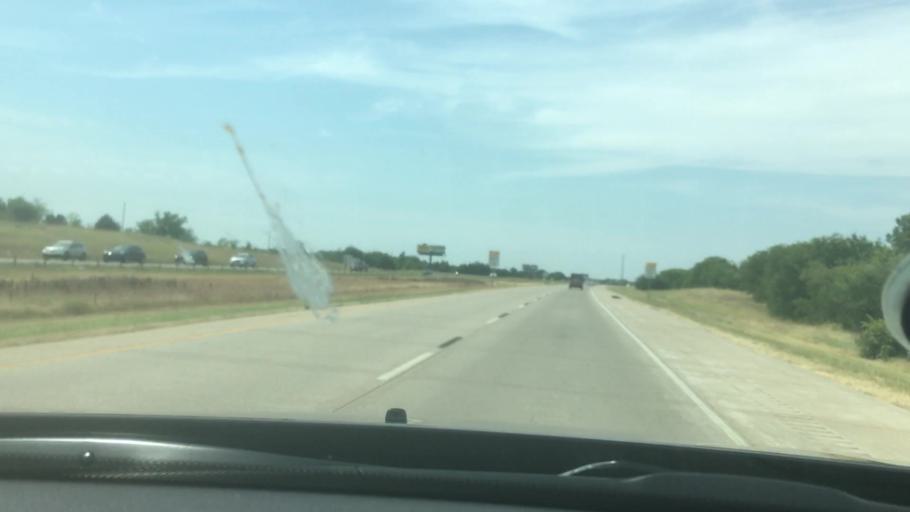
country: US
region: Oklahoma
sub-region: Carter County
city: Ardmore
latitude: 34.2925
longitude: -97.1595
